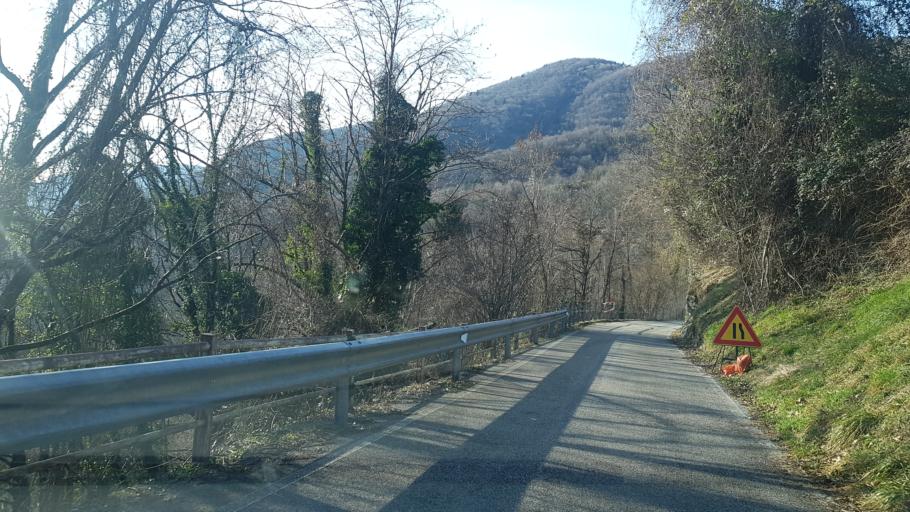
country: IT
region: Friuli Venezia Giulia
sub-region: Provincia di Udine
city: Clodig
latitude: 46.1582
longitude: 13.5880
